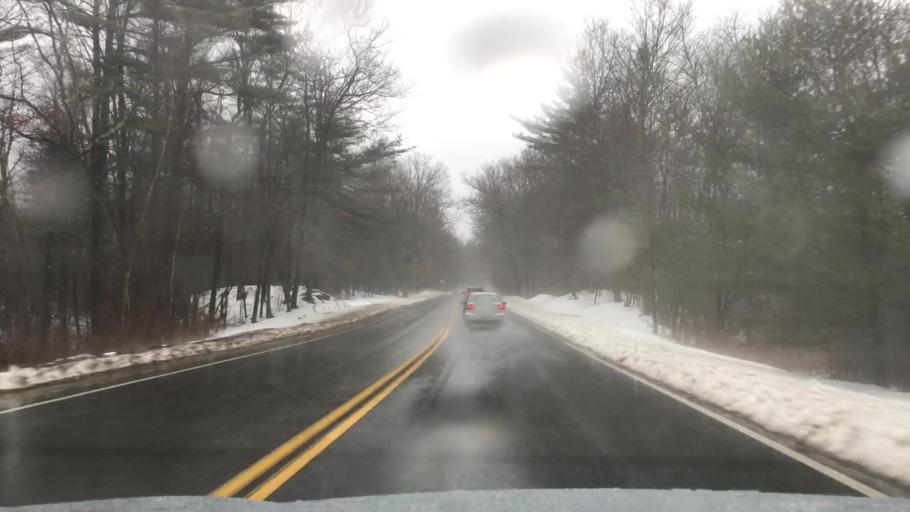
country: US
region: Massachusetts
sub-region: Hampshire County
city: Granby
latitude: 42.2364
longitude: -72.4847
